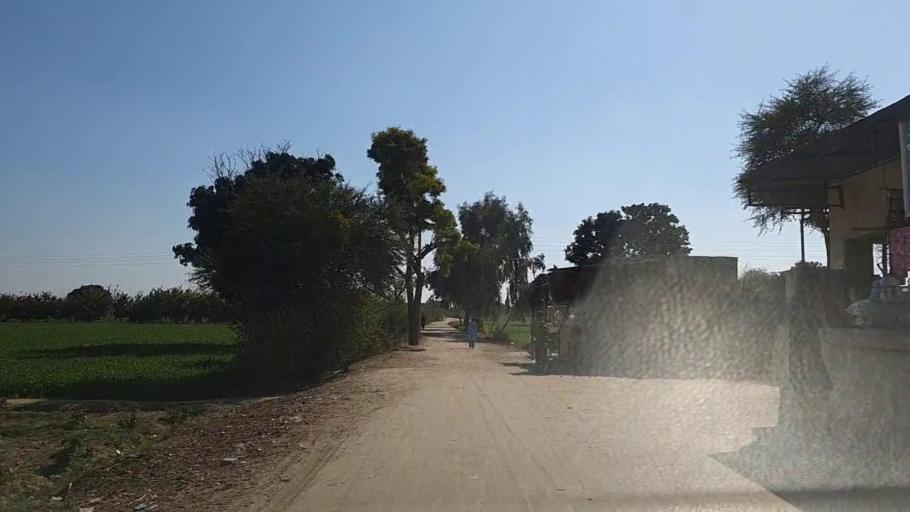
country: PK
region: Sindh
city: Nawabshah
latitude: 26.2346
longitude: 68.4457
